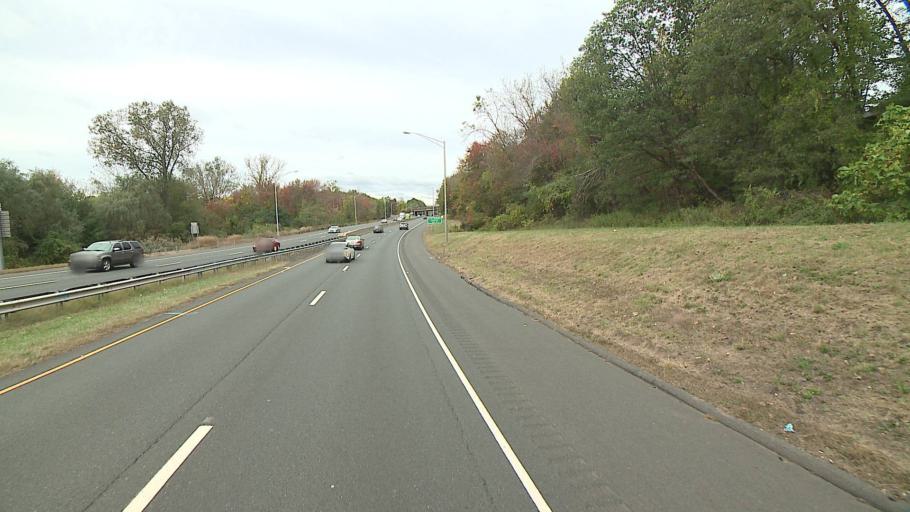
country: US
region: Connecticut
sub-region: Middlesex County
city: Middletown
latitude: 41.5396
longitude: -72.6243
